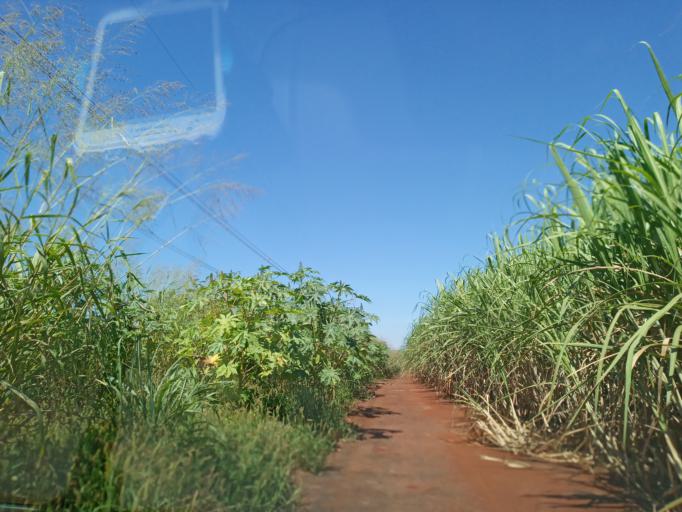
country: BR
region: Goias
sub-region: Itumbiara
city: Itumbiara
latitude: -18.4427
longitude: -49.1382
